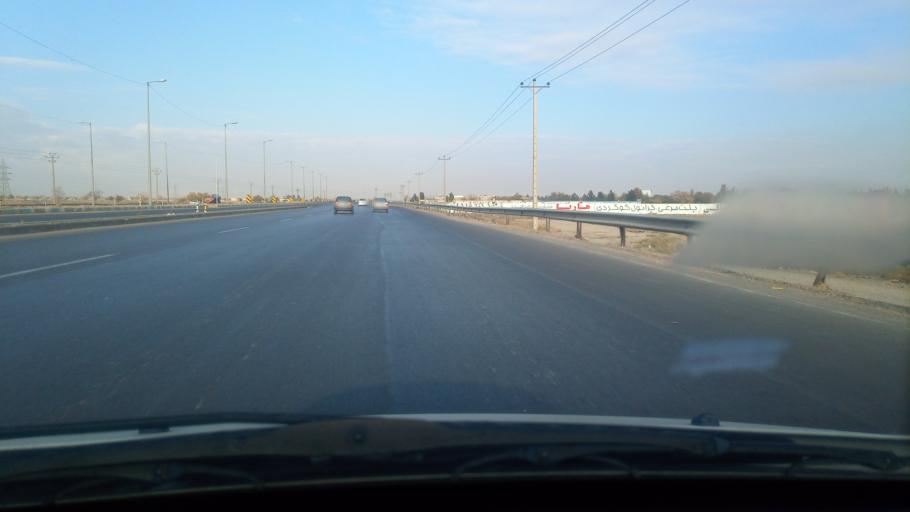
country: IR
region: Razavi Khorasan
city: Chenaran
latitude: 36.5275
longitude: 59.3030
